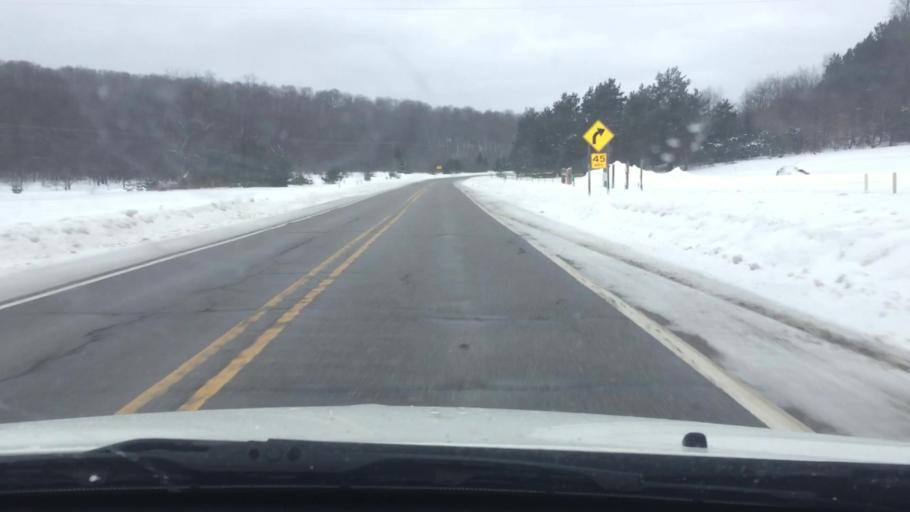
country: US
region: Michigan
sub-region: Charlevoix County
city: Boyne City
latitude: 45.0812
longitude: -84.9173
